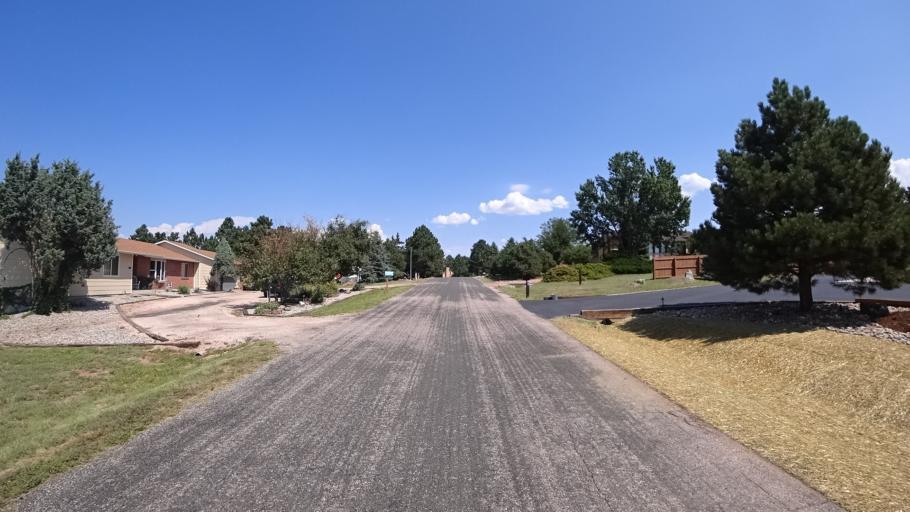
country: US
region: Colorado
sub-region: El Paso County
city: Air Force Academy
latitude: 38.9371
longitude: -104.7860
